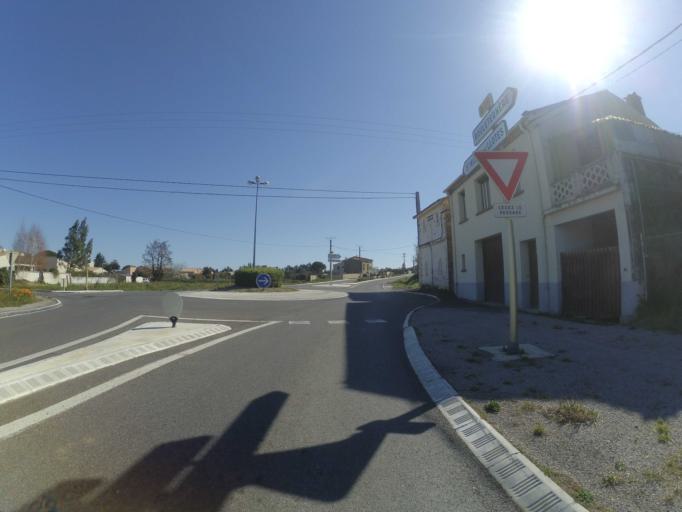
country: FR
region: Languedoc-Roussillon
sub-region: Departement des Pyrenees-Orientales
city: Ille-sur-Tet
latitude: 42.6559
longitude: 2.6217
